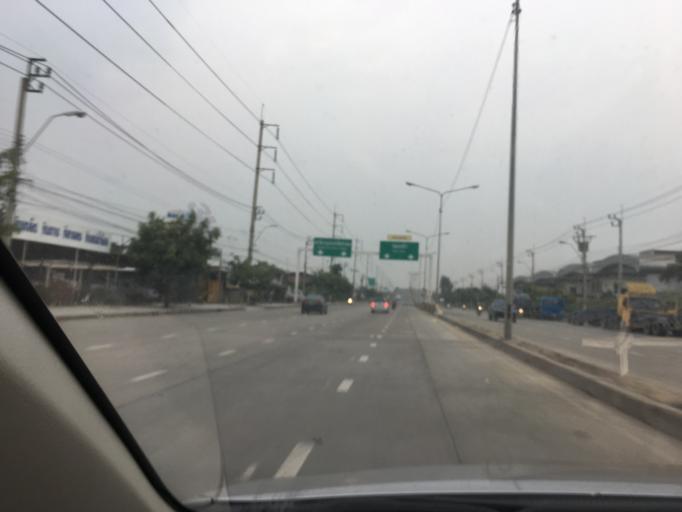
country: TH
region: Bangkok
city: Lat Krabang
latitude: 13.7543
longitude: 100.7650
